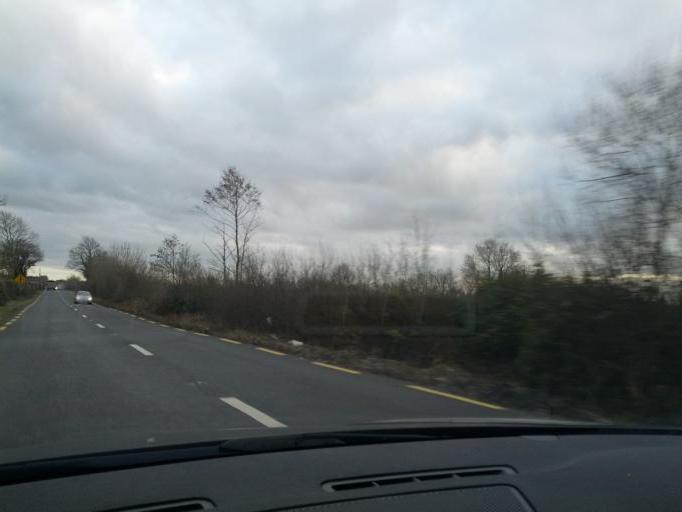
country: IE
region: Leinster
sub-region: Uibh Fhaili
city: Ferbane
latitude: 53.2018
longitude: -7.8837
